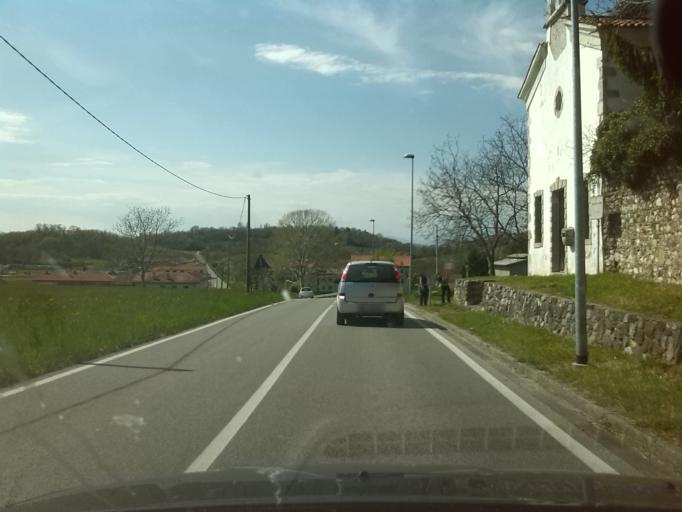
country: IT
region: Friuli Venezia Giulia
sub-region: Provincia di Udine
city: Moruzzo
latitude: 46.1166
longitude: 13.1158
